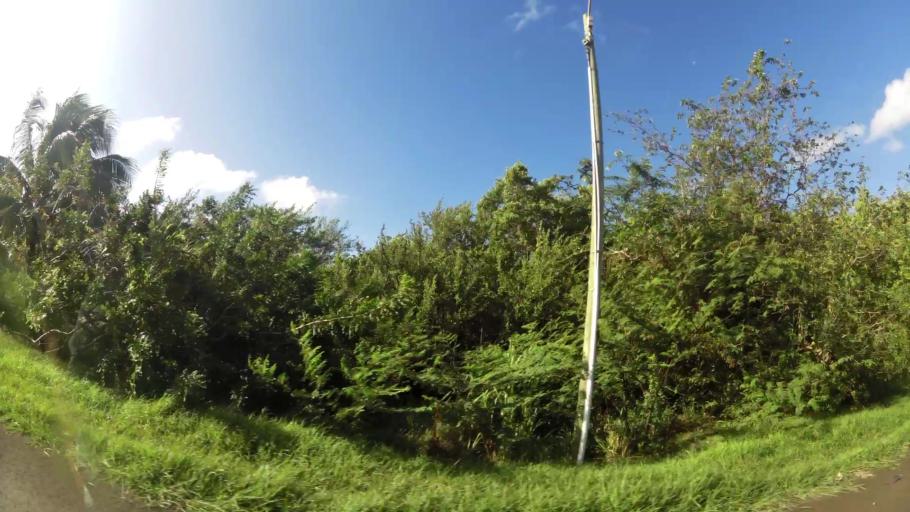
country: MQ
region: Martinique
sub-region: Martinique
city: Le Francois
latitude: 14.6201
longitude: -60.9020
